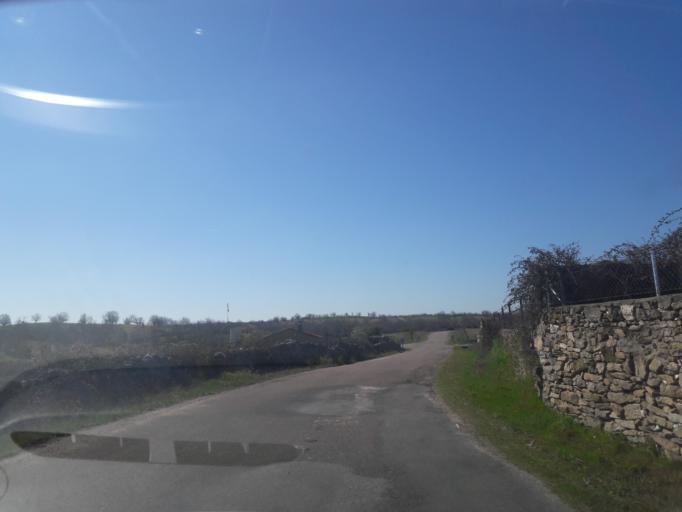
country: ES
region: Castille and Leon
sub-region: Provincia de Salamanca
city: Valsalabroso
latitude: 41.1503
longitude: -6.4861
